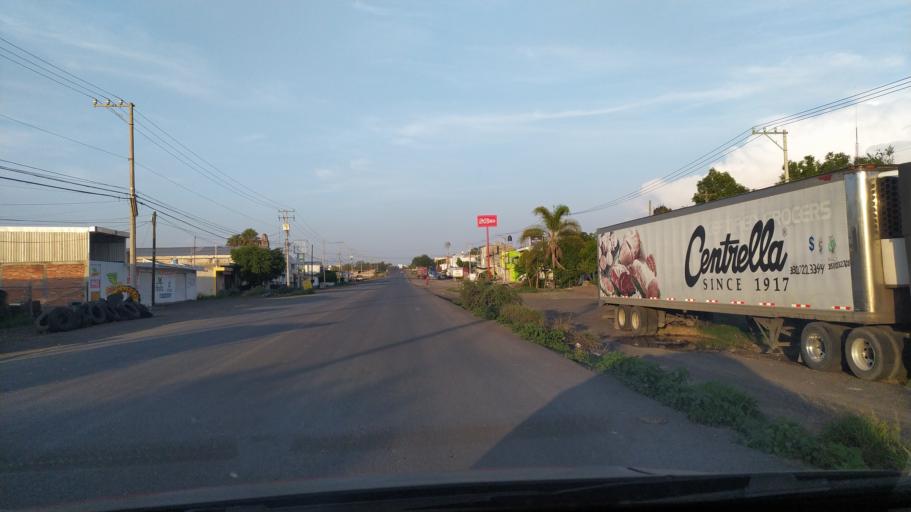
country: MX
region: Michoacan
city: Vistahermosa de Negrete
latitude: 20.2662
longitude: -102.4719
